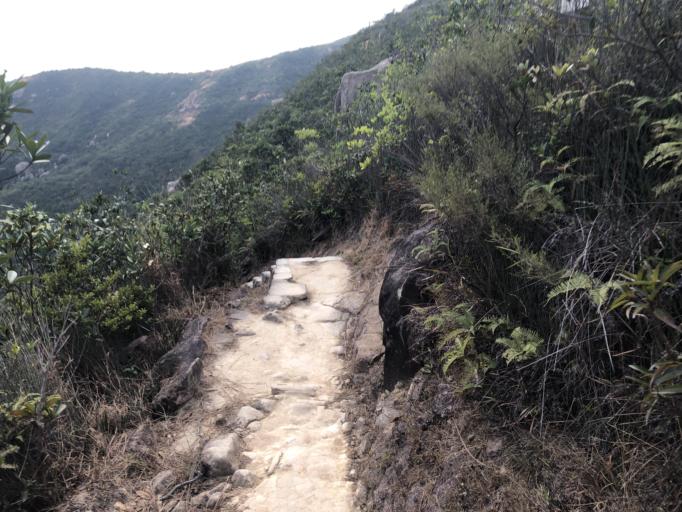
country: HK
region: Wanchai
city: Wan Chai
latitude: 22.2680
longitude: 114.2053
